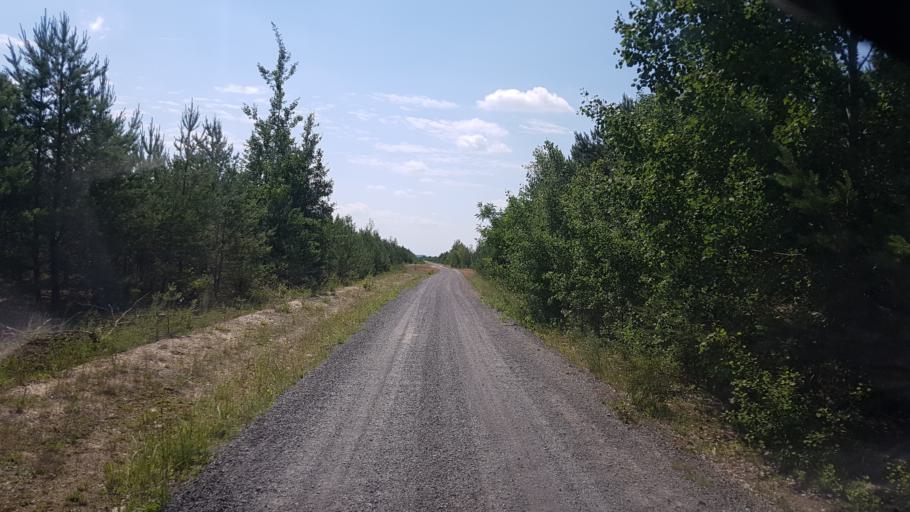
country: DE
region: Brandenburg
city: Sallgast
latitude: 51.5882
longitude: 13.7972
